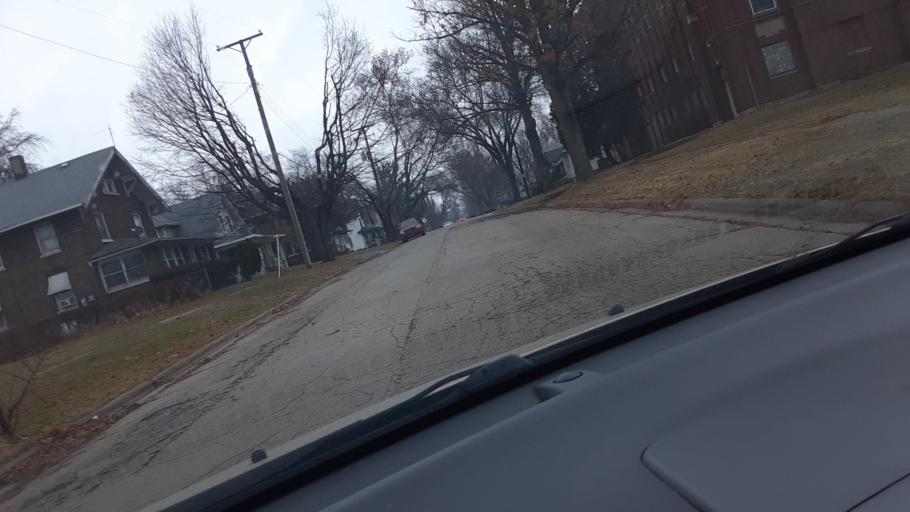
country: US
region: Illinois
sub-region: Winnebago County
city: Rockford
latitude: 42.2765
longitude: -89.1208
